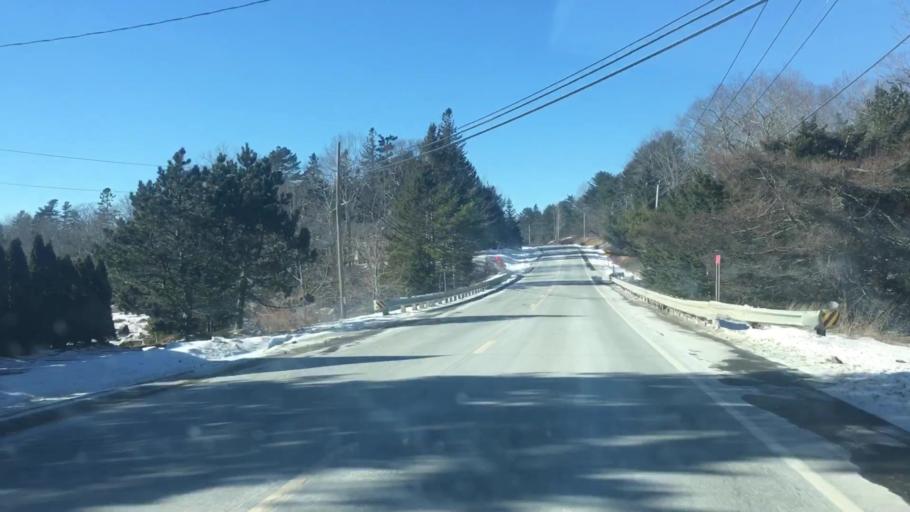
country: US
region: Maine
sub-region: Hancock County
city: Surry
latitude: 44.4940
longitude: -68.4663
